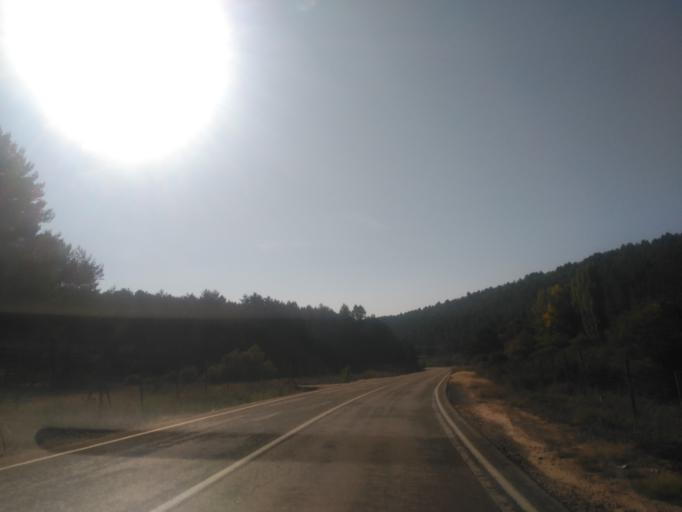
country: ES
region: Castille and Leon
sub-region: Provincia de Soria
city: San Leonardo de Yague
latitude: 41.8171
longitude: -3.0673
